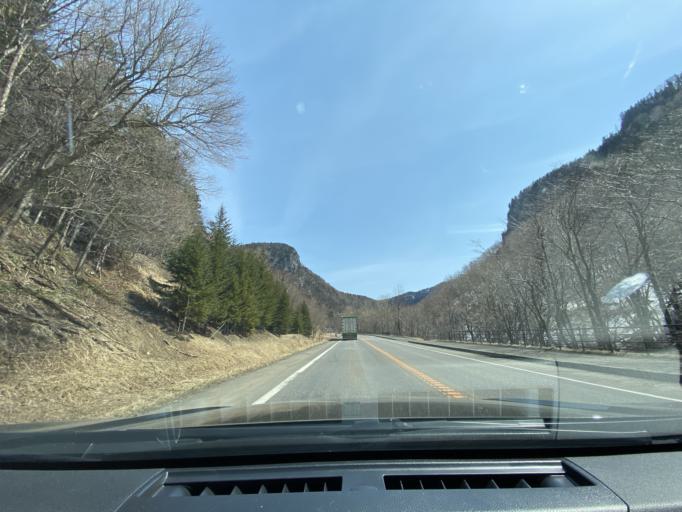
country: JP
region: Hokkaido
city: Kamikawa
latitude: 43.7258
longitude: 142.9669
